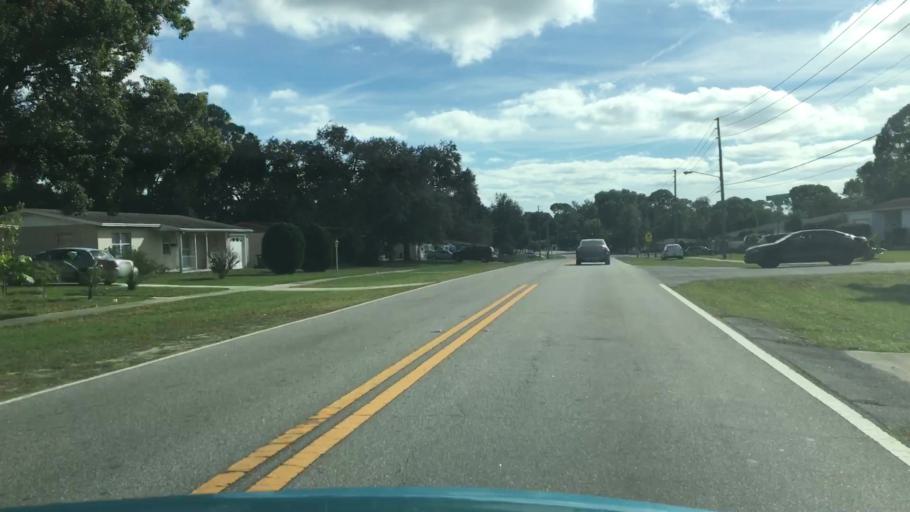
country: US
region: Florida
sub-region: Volusia County
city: Deltona
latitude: 28.9029
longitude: -81.2635
